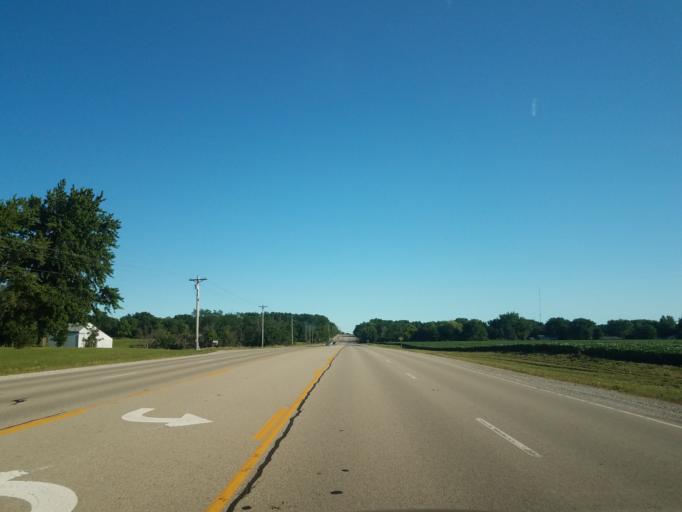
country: US
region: Illinois
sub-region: McLean County
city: Downs
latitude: 40.4291
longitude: -88.9015
